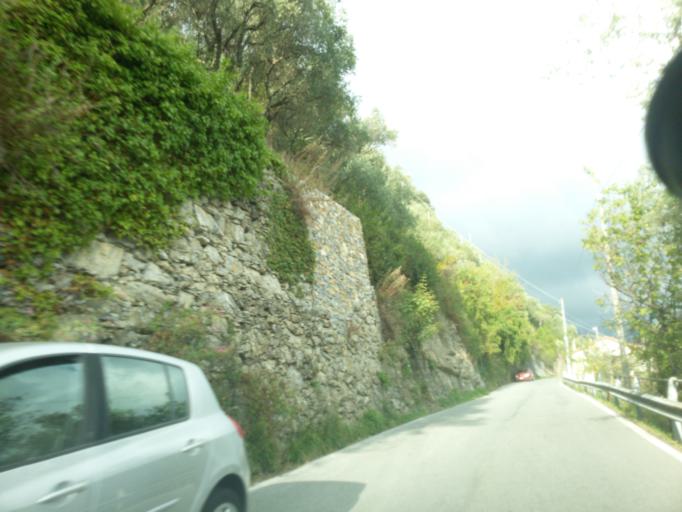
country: IT
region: Liguria
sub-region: Provincia di Genova
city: Camogli
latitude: 44.3562
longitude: 9.1711
